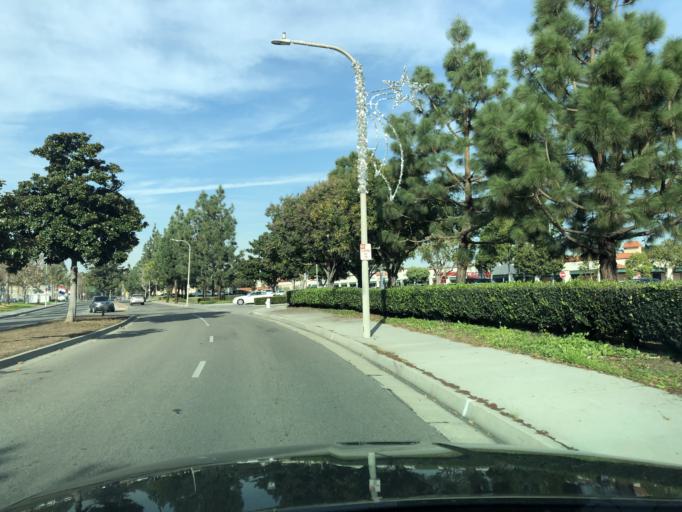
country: US
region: California
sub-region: Orange County
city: Santa Ana
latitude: 33.6964
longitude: -117.8888
